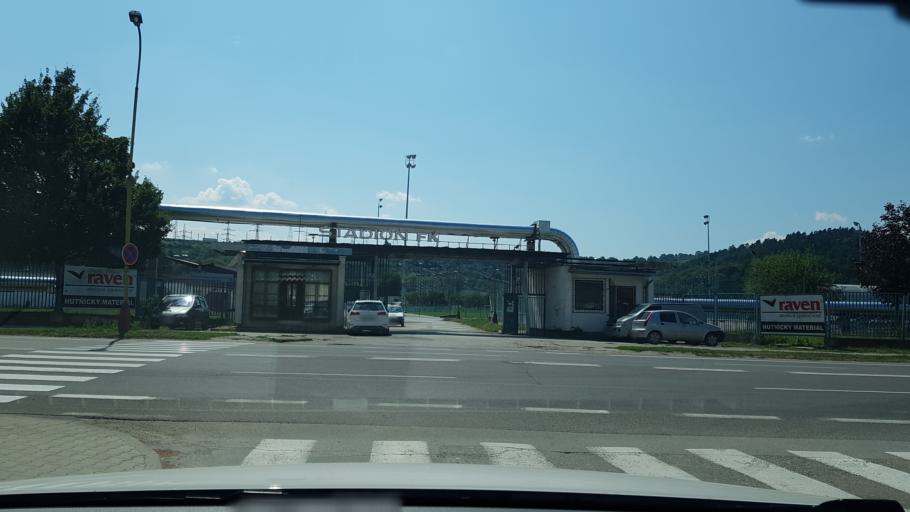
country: SK
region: Trenciansky
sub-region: Okres Povazska Bystrica
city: Povazska Bystrica
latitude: 49.1187
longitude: 18.4285
